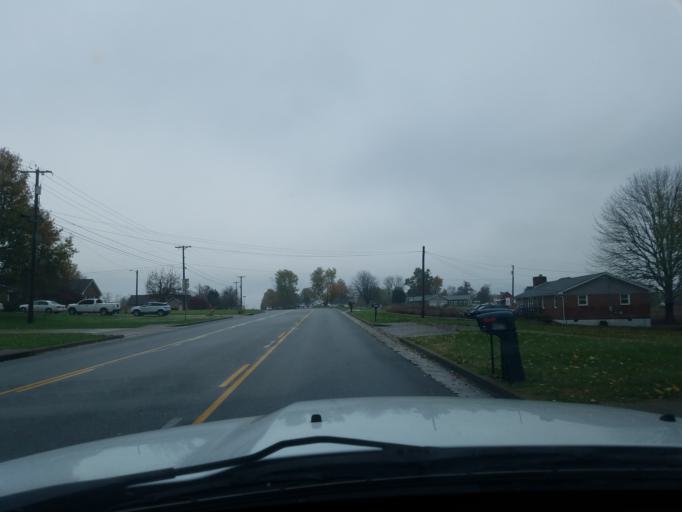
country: US
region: Kentucky
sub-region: Larue County
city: Hodgenville
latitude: 37.5551
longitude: -85.7154
